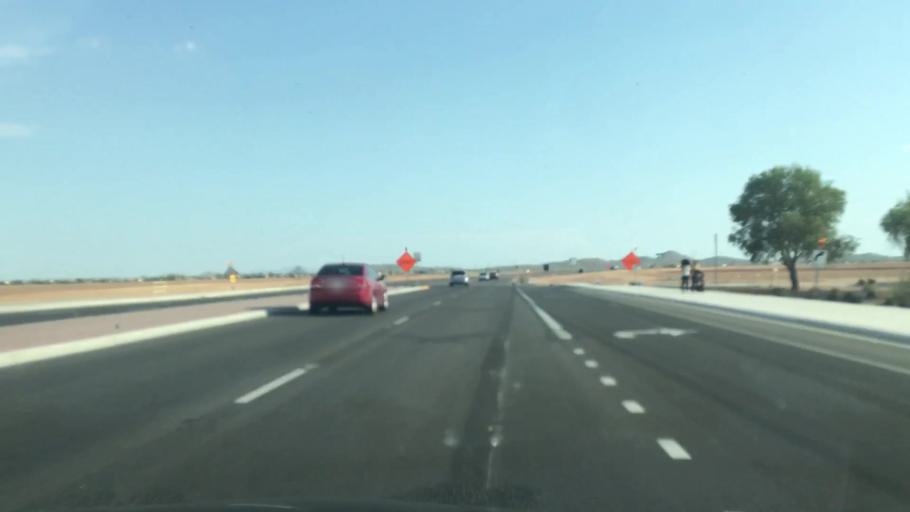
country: US
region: Arizona
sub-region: Pinal County
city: San Tan Valley
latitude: 33.1554
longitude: -111.5446
